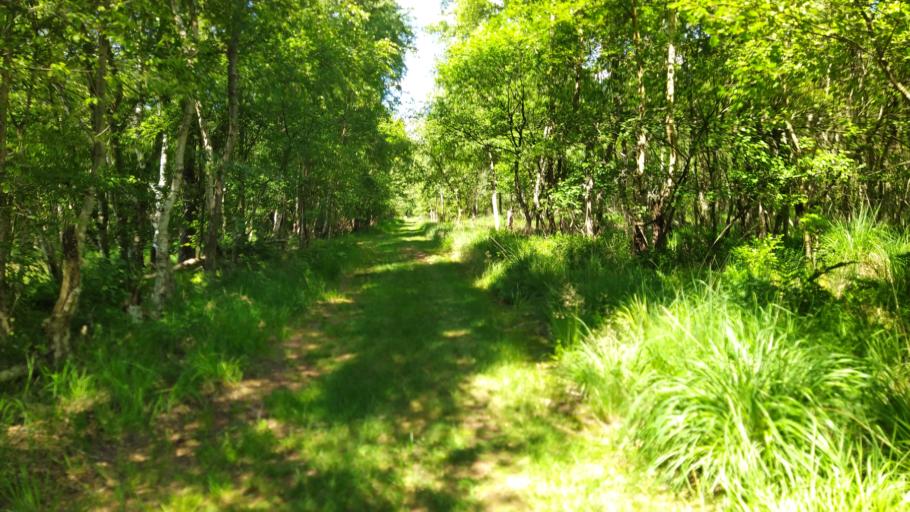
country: DE
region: Lower Saxony
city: Oldendorf
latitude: 53.5585
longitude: 9.2556
